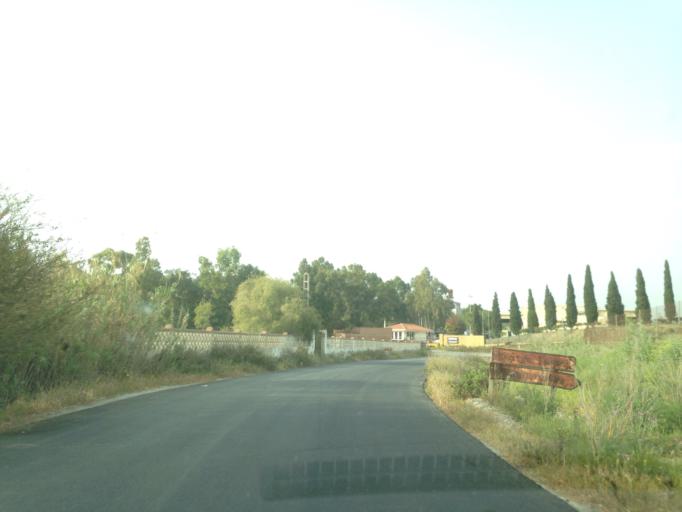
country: ES
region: Andalusia
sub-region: Provincia de Malaga
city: Estacion de Cartama
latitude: 36.7431
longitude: -4.5651
